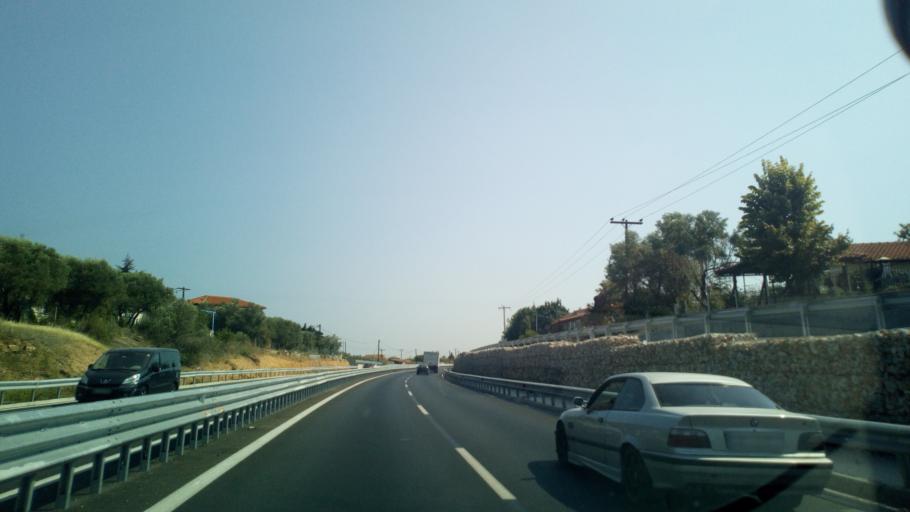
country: GR
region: Central Macedonia
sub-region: Nomos Chalkidikis
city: Nea Potidhaia
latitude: 40.2186
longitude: 23.3193
